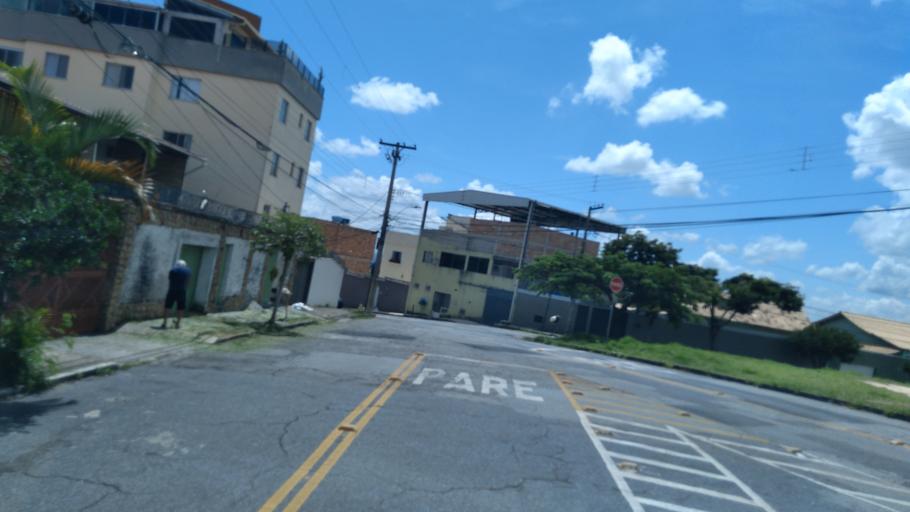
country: BR
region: Minas Gerais
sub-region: Belo Horizonte
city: Belo Horizonte
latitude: -19.8699
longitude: -43.9165
